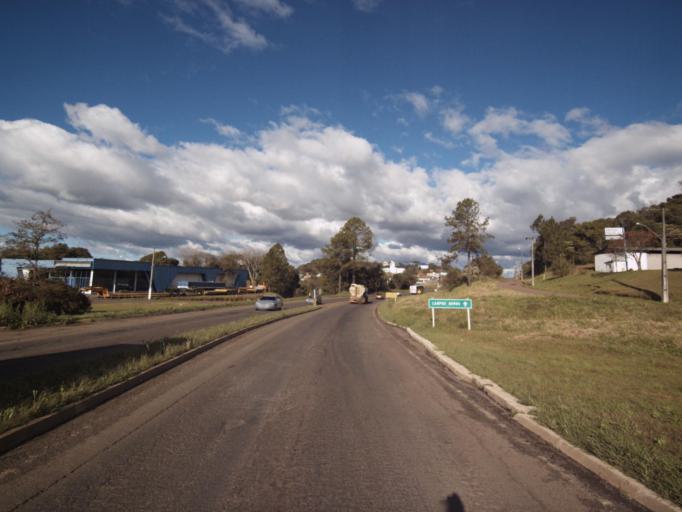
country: BR
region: Santa Catarina
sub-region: Joacaba
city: Joacaba
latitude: -27.1766
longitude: -51.5259
